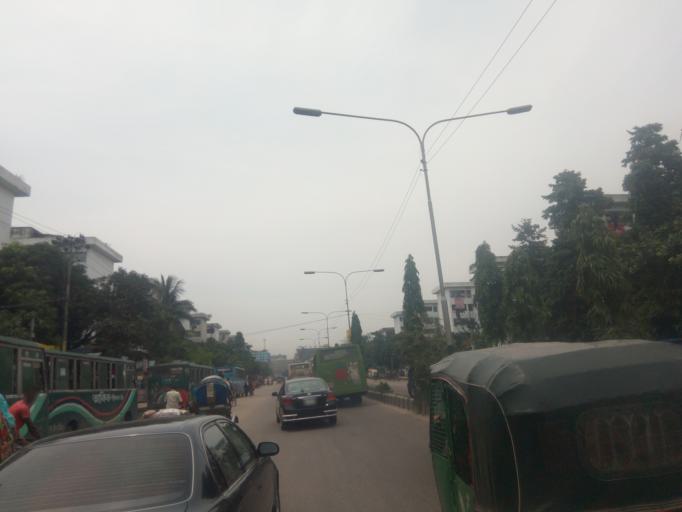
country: BD
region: Dhaka
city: Azimpur
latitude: 23.7895
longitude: 90.3538
